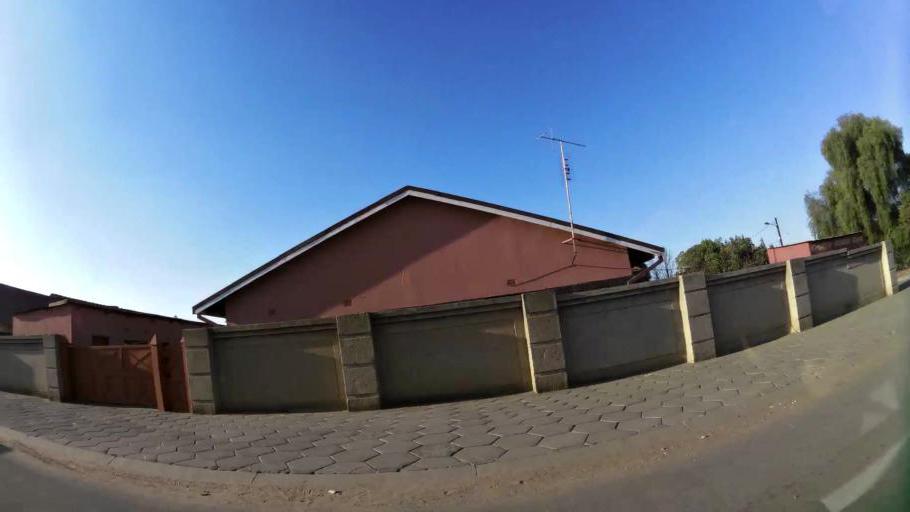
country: ZA
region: North-West
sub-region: Bojanala Platinum District Municipality
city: Rustenburg
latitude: -25.6405
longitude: 27.2206
